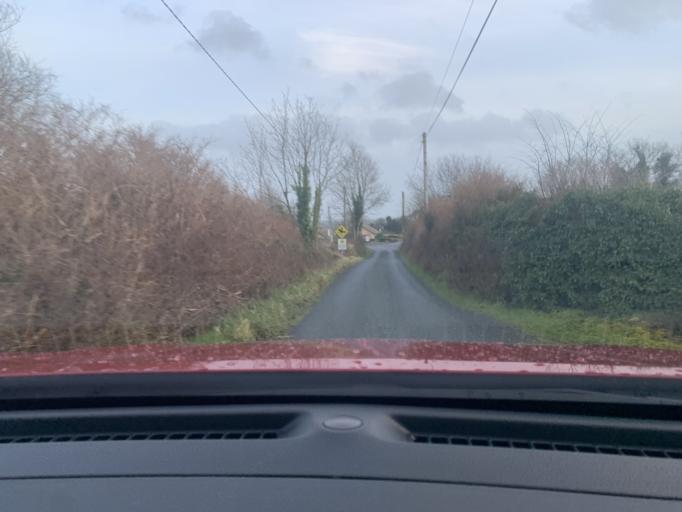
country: IE
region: Connaught
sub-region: Roscommon
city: Ballaghaderreen
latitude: 53.9438
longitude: -8.4988
